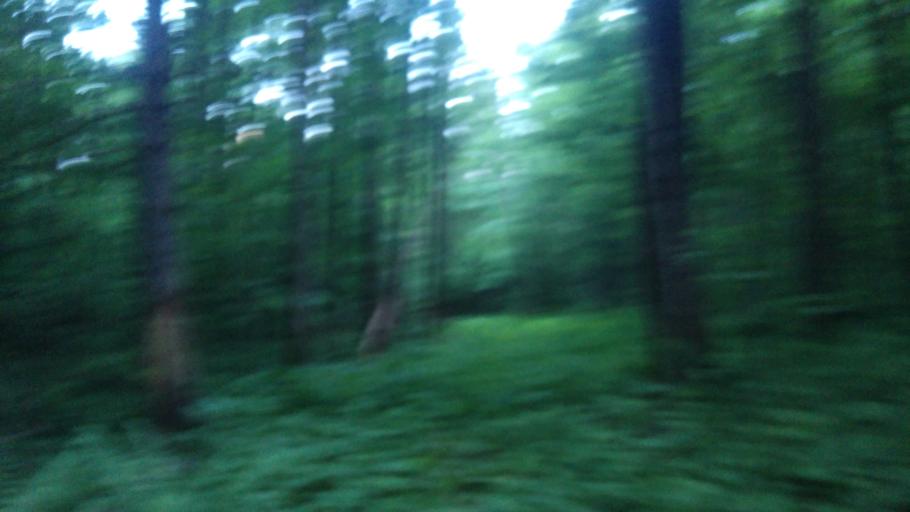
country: RU
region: Perm
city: Ferma
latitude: 57.9644
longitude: 56.3431
